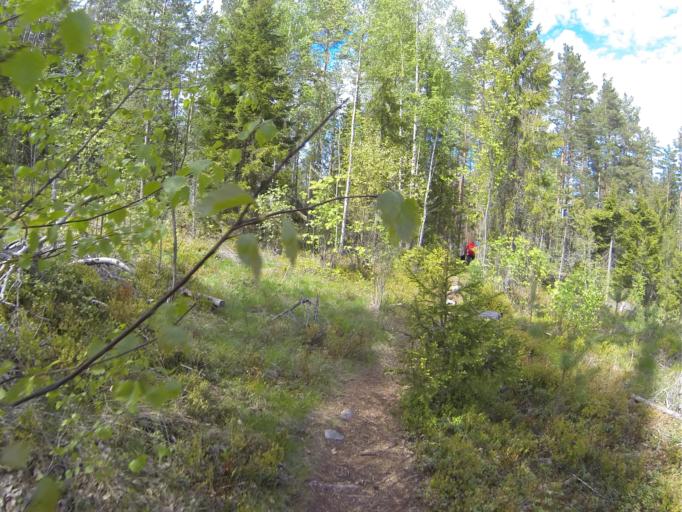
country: FI
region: Varsinais-Suomi
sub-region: Salo
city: Halikko
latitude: 60.3467
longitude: 23.0902
